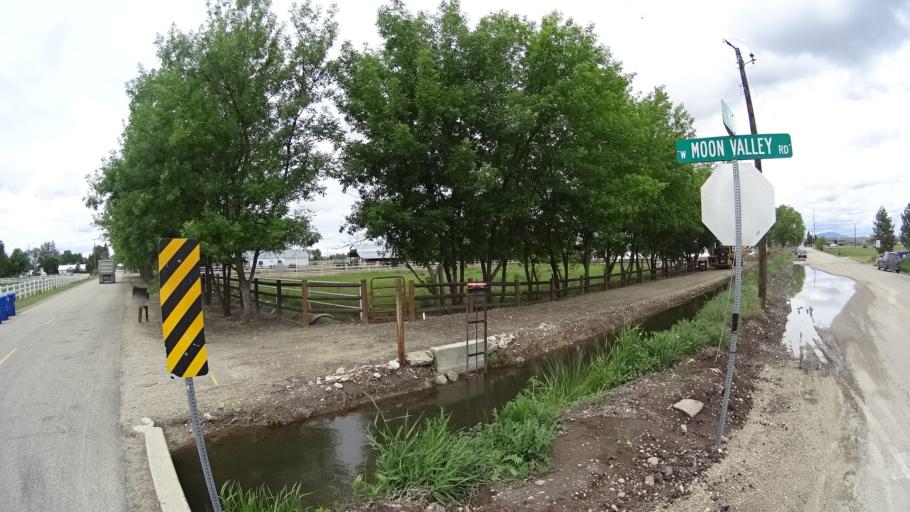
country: US
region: Idaho
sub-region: Ada County
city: Star
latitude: 43.6892
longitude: -116.4435
